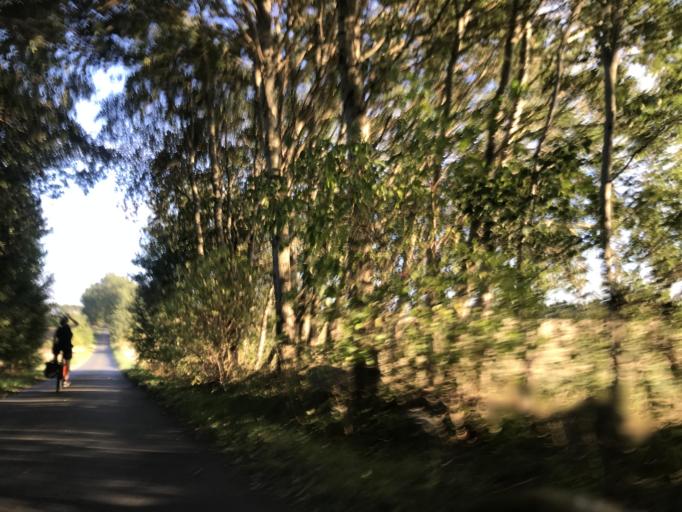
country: DE
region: Lower Saxony
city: Reinstorf
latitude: 53.2346
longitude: 10.5931
